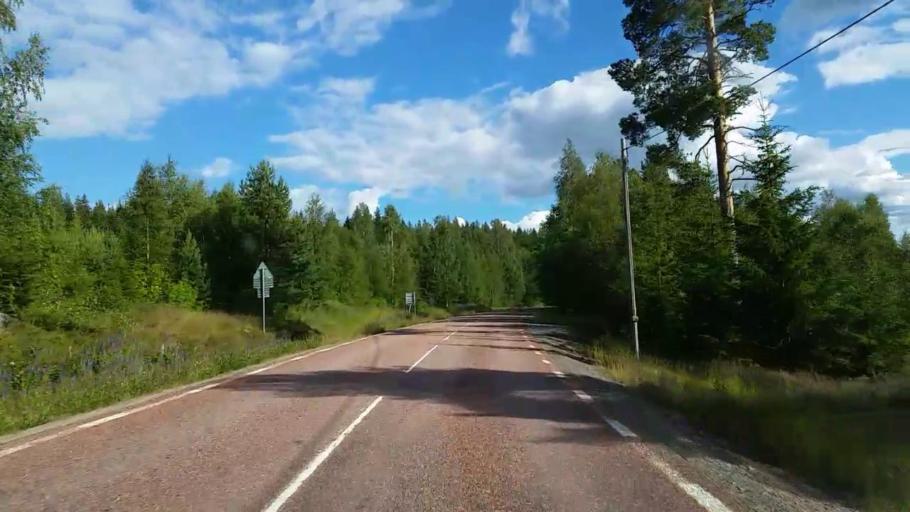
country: SE
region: Vaesternorrland
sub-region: Ange Kommun
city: Ange
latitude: 62.1527
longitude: 15.6805
